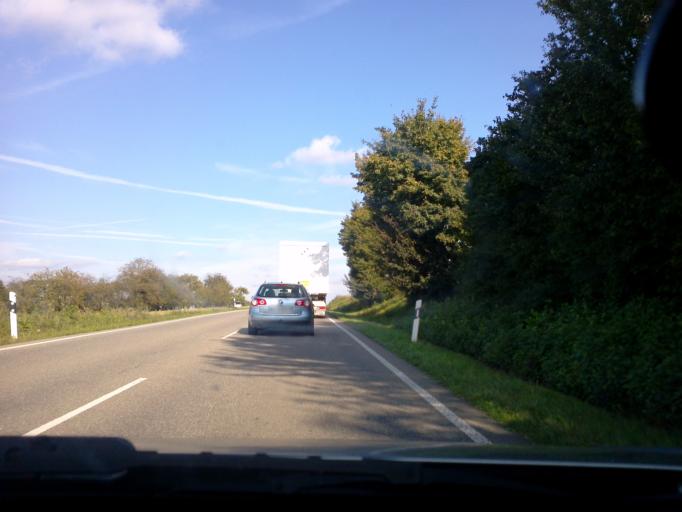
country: DE
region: Baden-Wuerttemberg
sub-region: Karlsruhe Region
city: Sulzfeld
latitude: 49.1194
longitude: 8.8401
